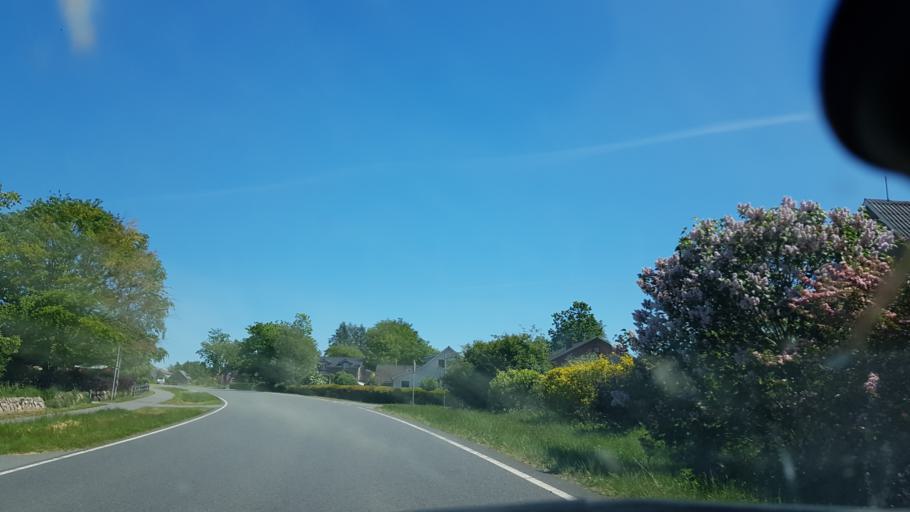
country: DE
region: Schleswig-Holstein
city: Klixbull
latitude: 54.7936
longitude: 8.9062
